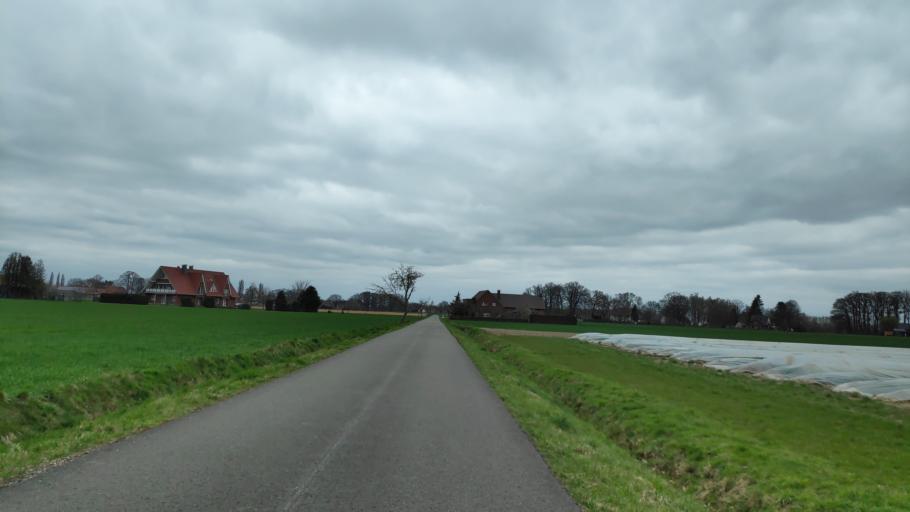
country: DE
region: North Rhine-Westphalia
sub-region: Regierungsbezirk Detmold
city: Minden
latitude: 52.3258
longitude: 8.8566
